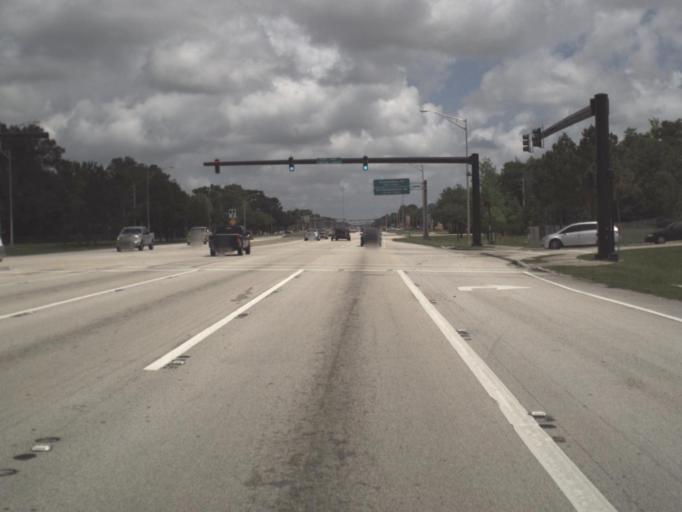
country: US
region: Florida
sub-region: Saint Johns County
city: Fruit Cove
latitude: 30.2137
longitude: -81.5518
